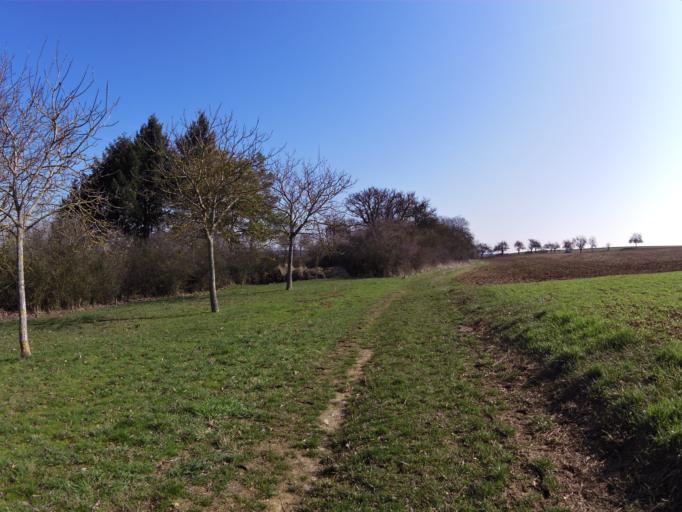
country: DE
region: Bavaria
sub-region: Regierungsbezirk Unterfranken
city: Estenfeld
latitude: 49.8190
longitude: 10.0083
